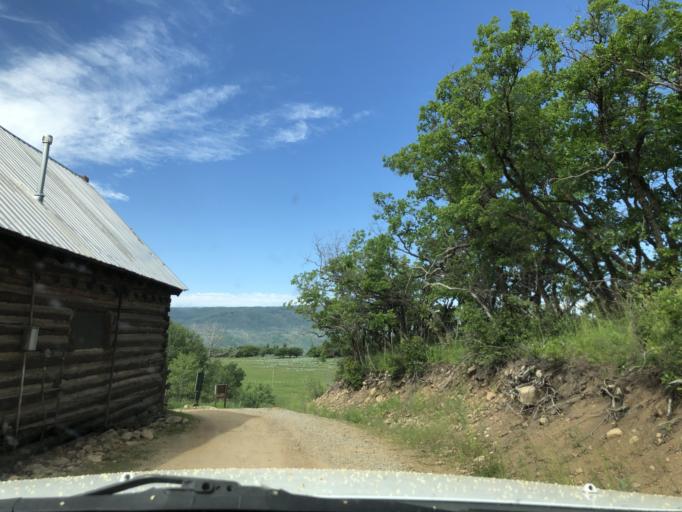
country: US
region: Colorado
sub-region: Delta County
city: Paonia
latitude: 39.0349
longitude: -107.3386
